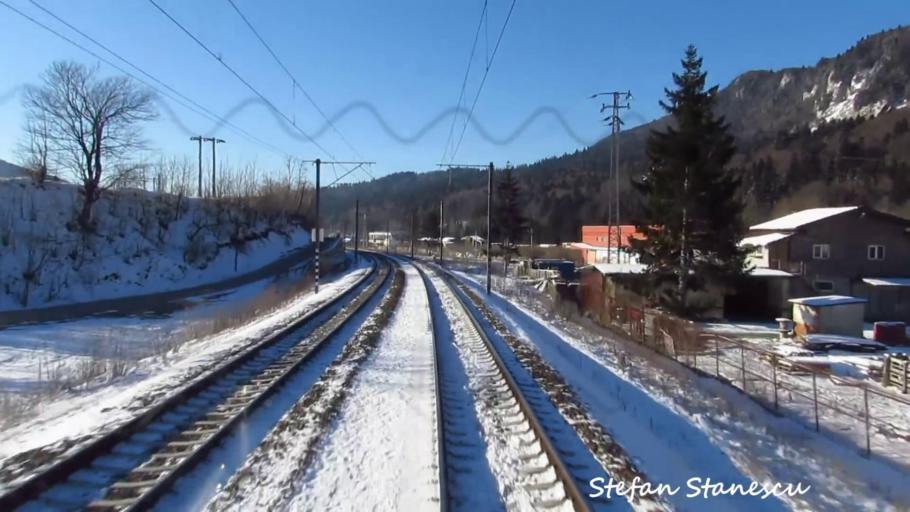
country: RO
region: Prahova
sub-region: Oras Busteni
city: Poiana Tapului
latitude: 45.3806
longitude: 25.5410
